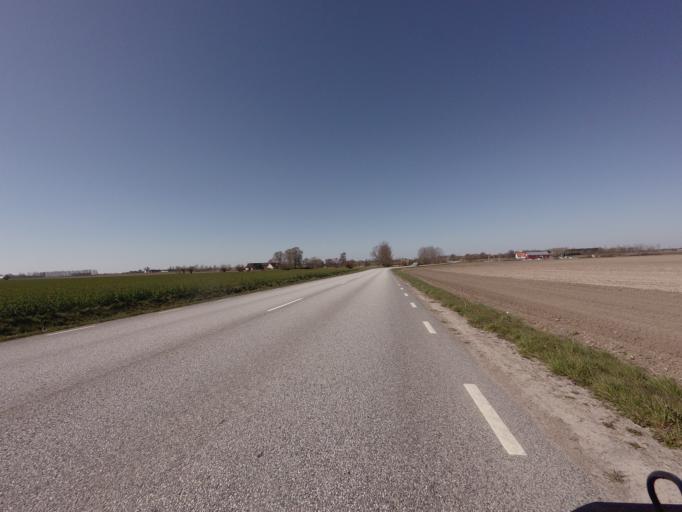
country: SE
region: Skane
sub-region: Malmo
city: Oxie
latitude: 55.4661
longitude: 13.0886
